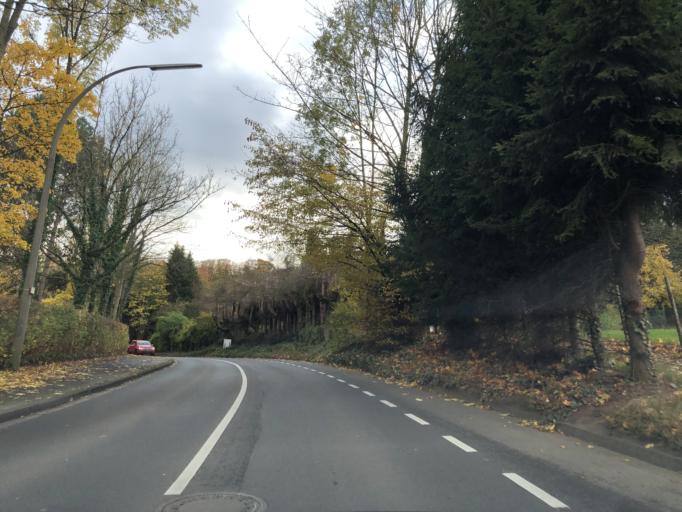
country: DE
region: North Rhine-Westphalia
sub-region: Regierungsbezirk Koln
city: Konigswinter
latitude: 50.6741
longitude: 7.1523
